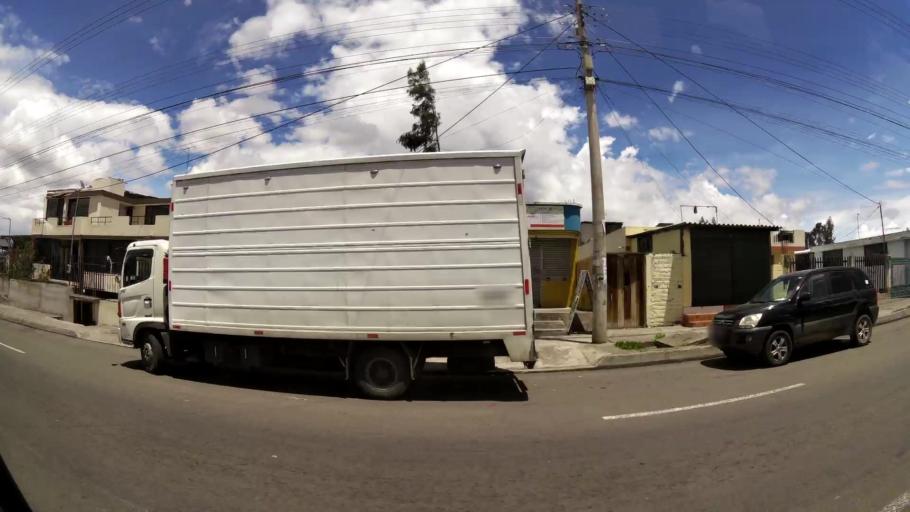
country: EC
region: Tungurahua
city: Ambato
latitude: -1.2759
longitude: -78.6105
